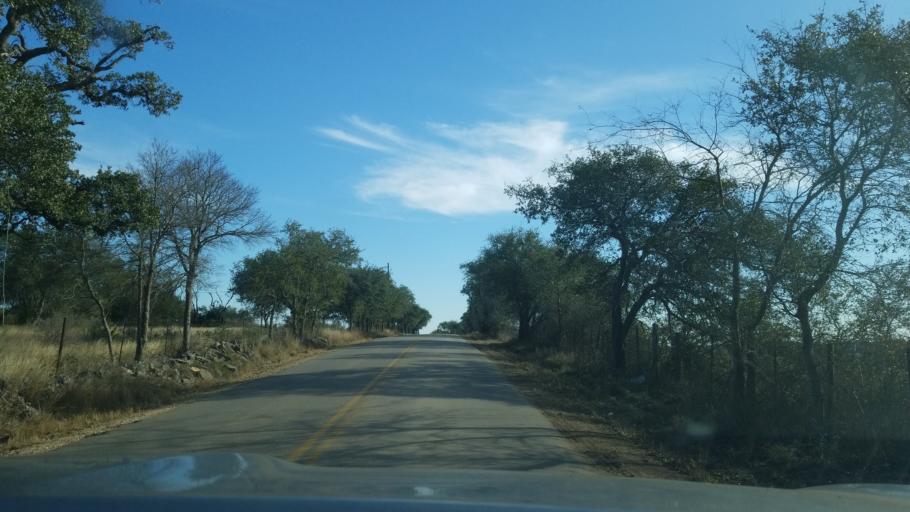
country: US
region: Texas
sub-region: Comal County
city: Canyon Lake
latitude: 29.7866
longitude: -98.2856
